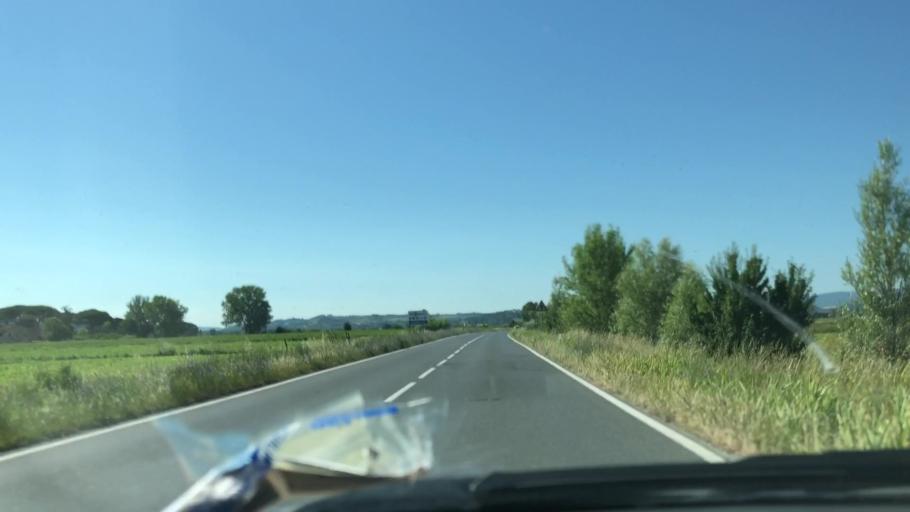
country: IT
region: Tuscany
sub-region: Province of Pisa
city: Forcoli
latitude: 43.5924
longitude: 10.6999
